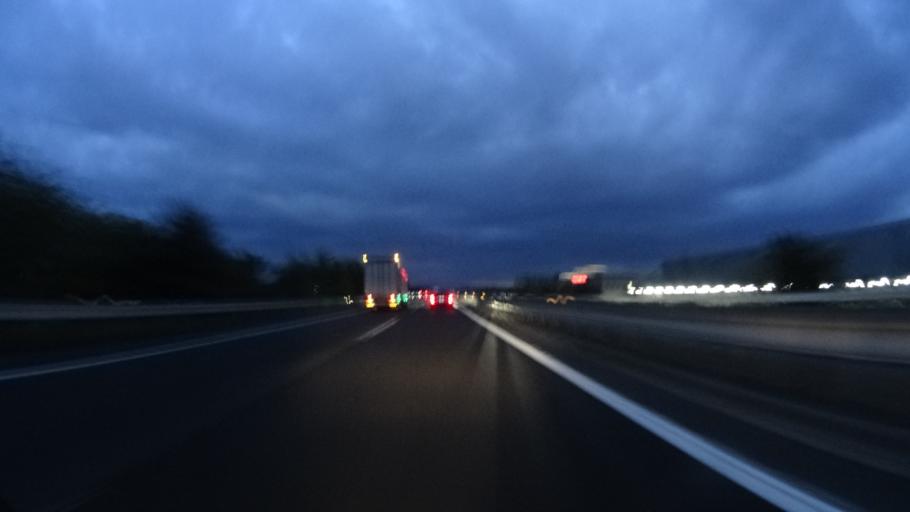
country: JP
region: Shiga Prefecture
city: Youkaichi
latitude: 35.1144
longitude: 136.2565
